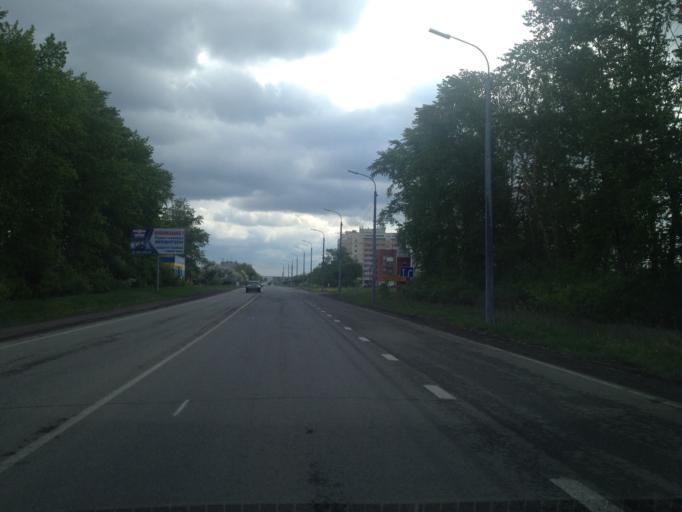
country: RU
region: Sverdlovsk
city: Aramil
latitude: 56.6953
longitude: 60.7878
